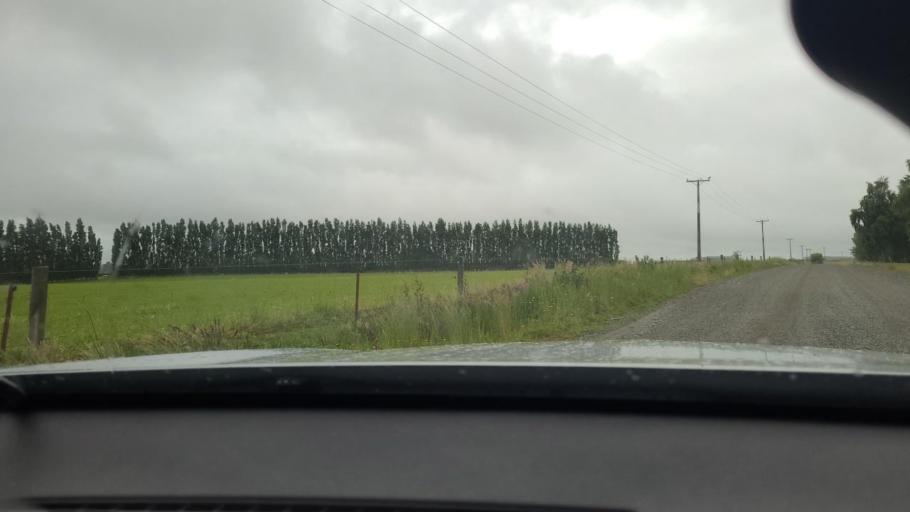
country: NZ
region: Southland
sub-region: Southland District
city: Riverton
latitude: -46.1292
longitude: 168.0071
